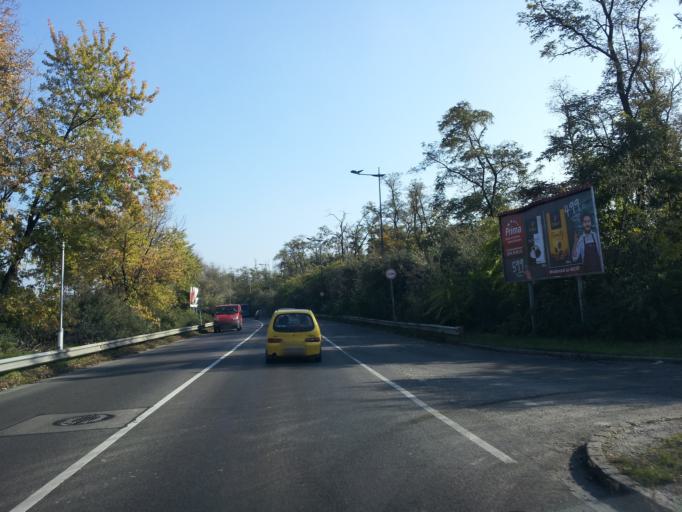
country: HU
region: Budapest
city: Budapest XIX. keruelet
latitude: 47.4626
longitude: 19.1513
